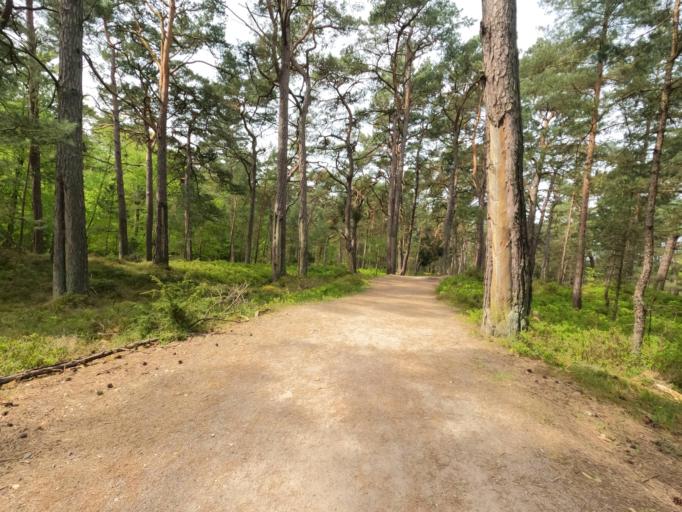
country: DE
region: Mecklenburg-Vorpommern
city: Ostseebad Prerow
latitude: 54.4508
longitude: 12.5490
